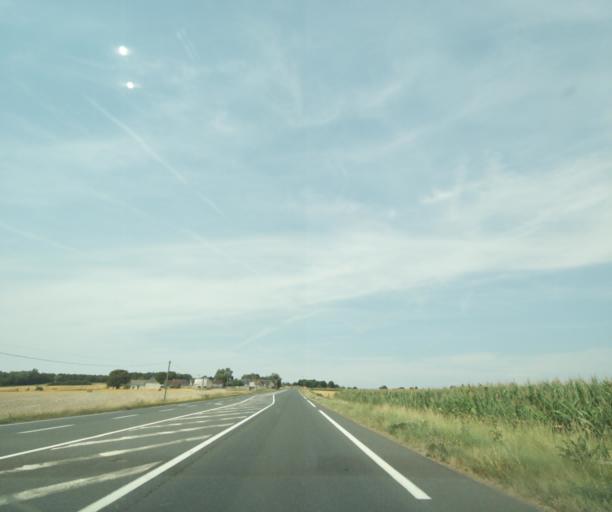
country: FR
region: Centre
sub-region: Departement d'Indre-et-Loire
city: La Celle-Saint-Avant
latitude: 47.0524
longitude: 0.6144
